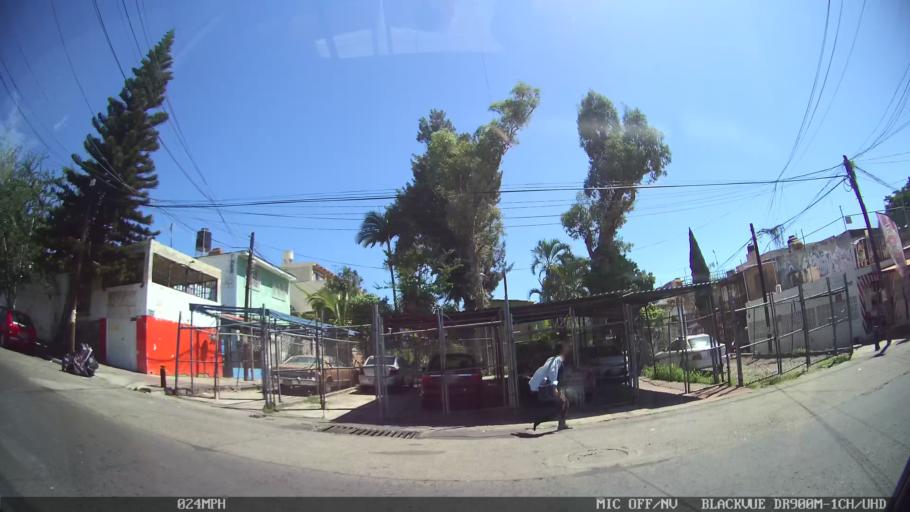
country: MX
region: Jalisco
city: Tlaquepaque
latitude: 20.6972
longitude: -103.2904
